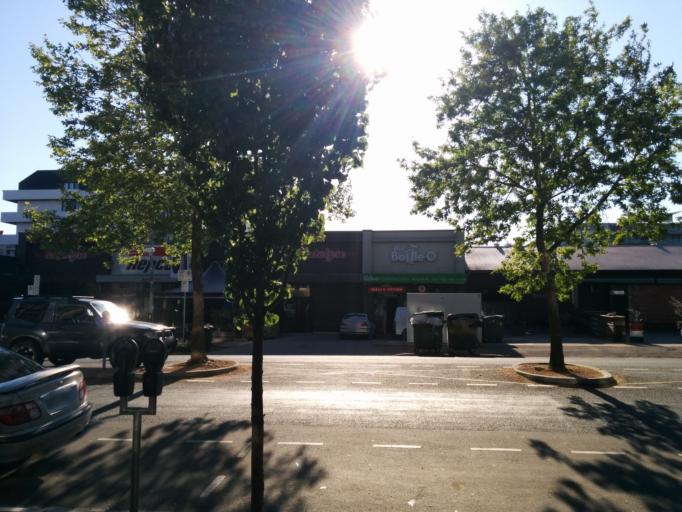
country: AU
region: Australian Capital Territory
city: Canberra
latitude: -35.2726
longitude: 149.1330
